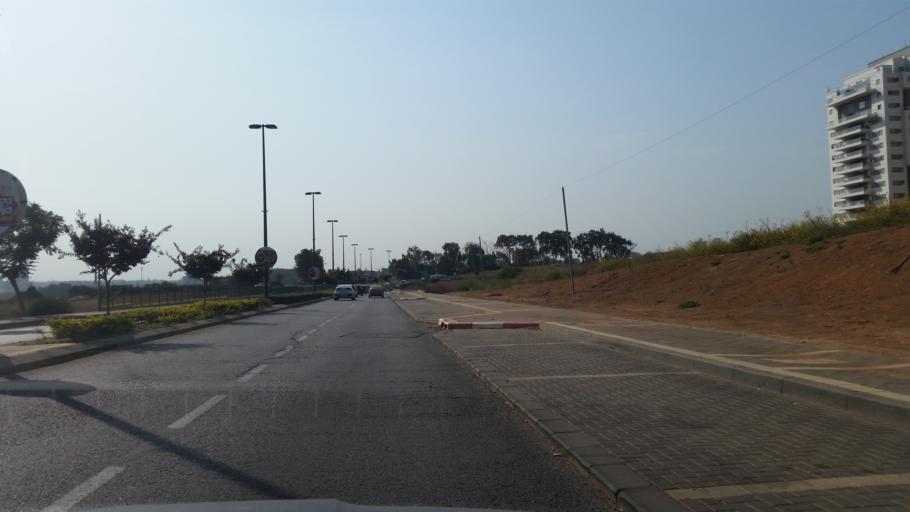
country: IL
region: Central District
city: Netanya
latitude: 32.3106
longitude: 34.8613
